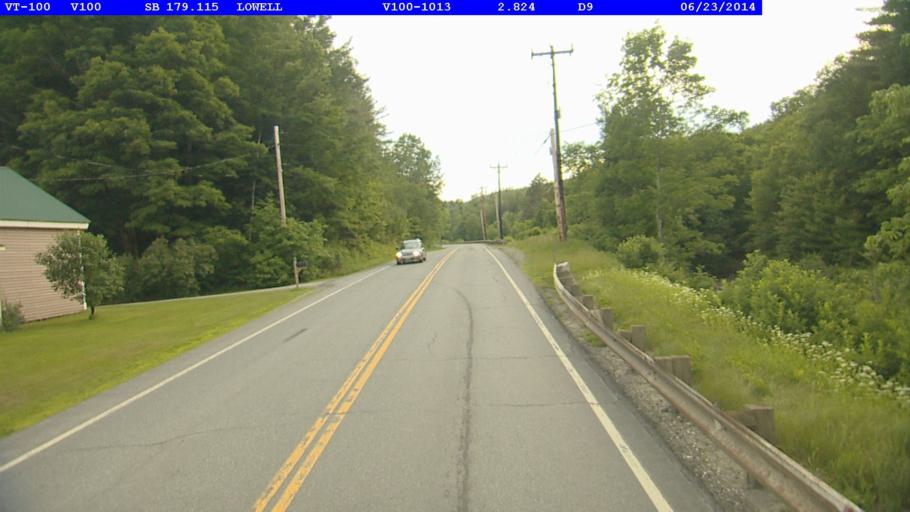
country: US
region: Vermont
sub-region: Lamoille County
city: Hyde Park
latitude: 44.7779
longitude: -72.4541
